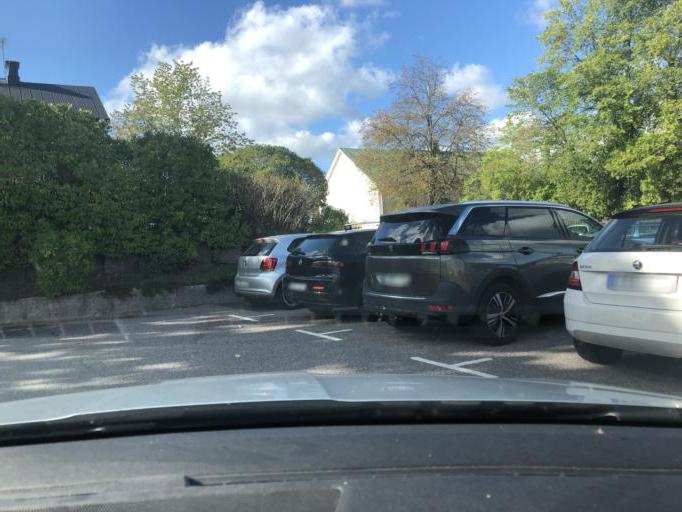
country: SE
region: Kalmar
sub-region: Vasterviks Kommun
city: Vaestervik
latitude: 57.7568
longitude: 16.6386
